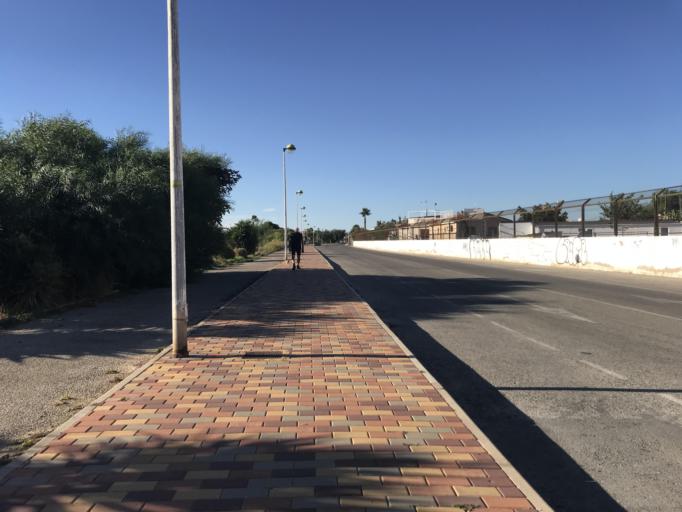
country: ES
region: Valencia
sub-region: Provincia de Alicante
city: Torrevieja
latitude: 37.9822
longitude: -0.6962
